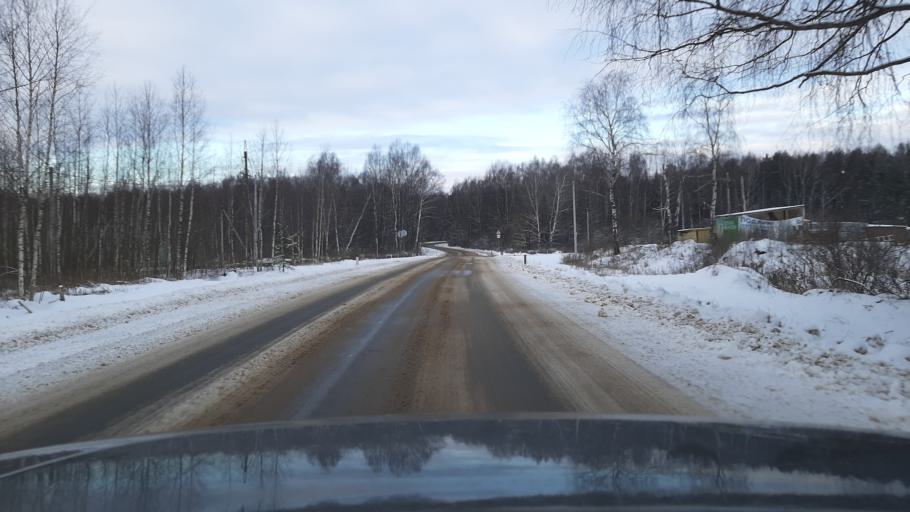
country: RU
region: Kostroma
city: Nerekhta
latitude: 57.4685
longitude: 40.6235
